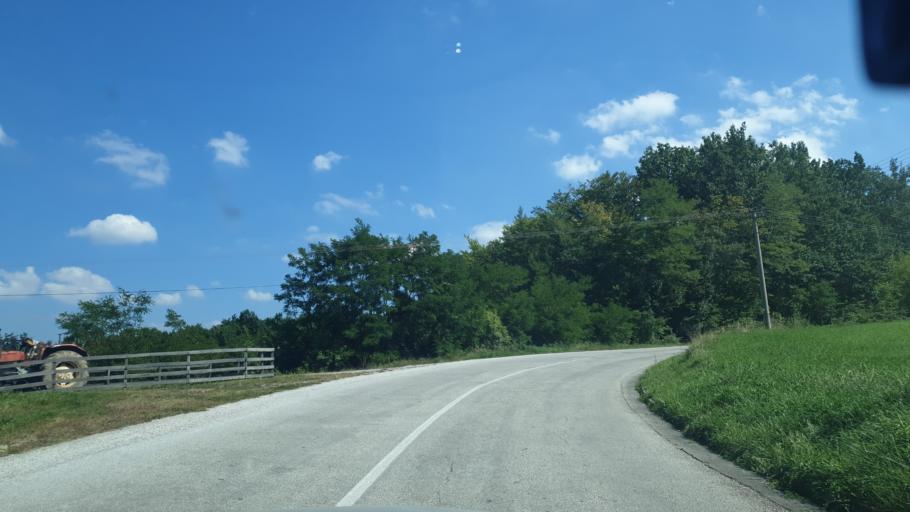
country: RS
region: Central Serbia
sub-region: Zlatiborski Okrug
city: Kosjeric
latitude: 44.0245
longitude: 20.0205
